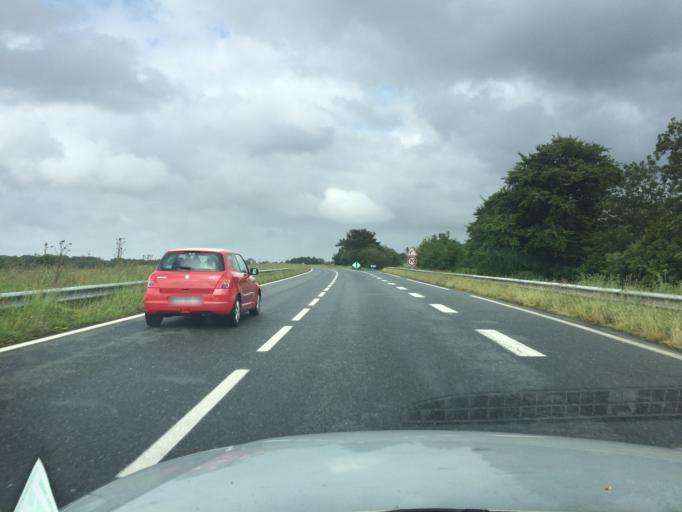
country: FR
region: Brittany
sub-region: Departement du Finistere
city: Guiclan
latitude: 48.5205
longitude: -4.0011
